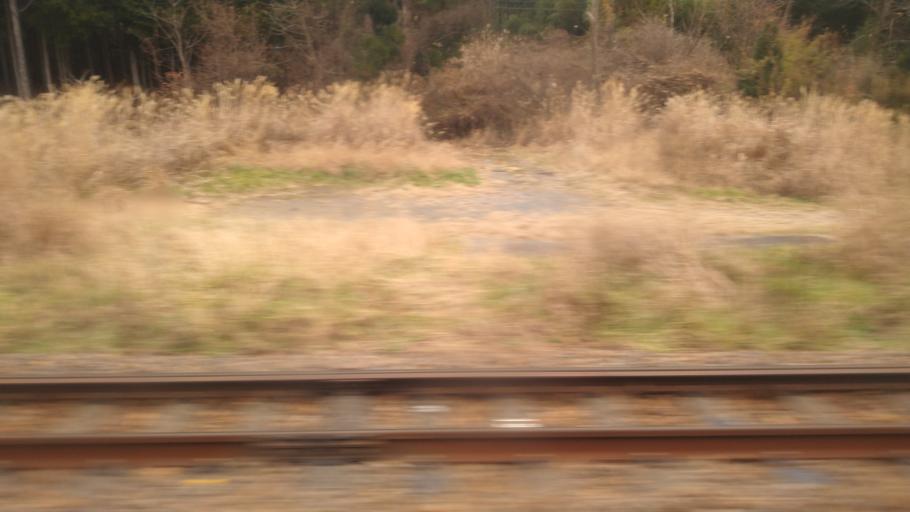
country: JP
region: Nagano
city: Ina
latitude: 35.8234
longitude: 137.6817
